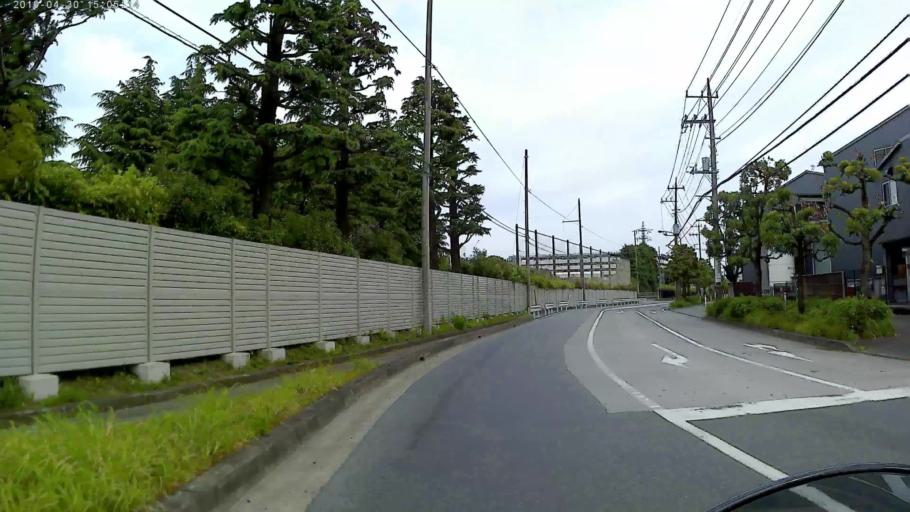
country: JP
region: Kanagawa
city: Zama
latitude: 35.5612
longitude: 139.3398
